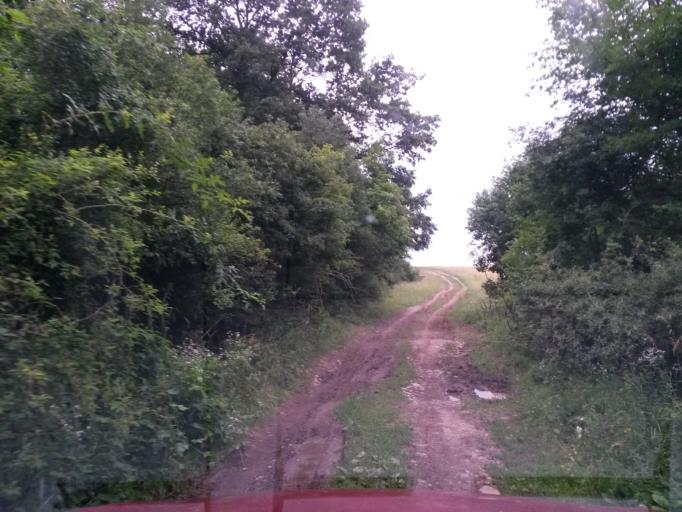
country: SK
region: Banskobystricky
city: Velky Krtis
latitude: 48.3129
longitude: 19.4180
